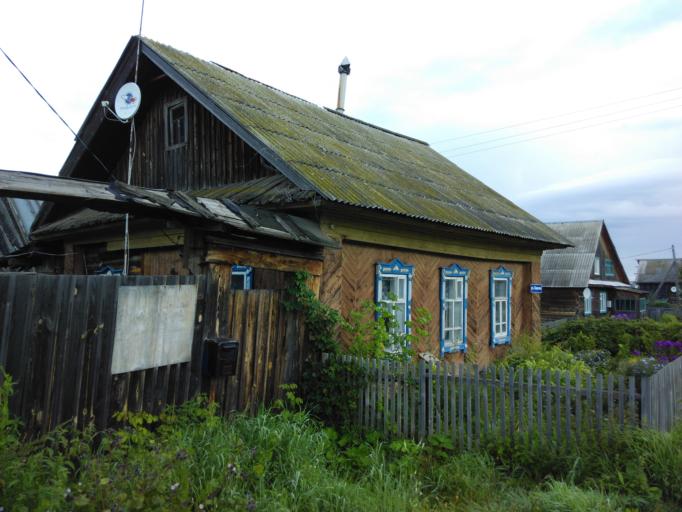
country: RU
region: Perm
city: Foki
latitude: 56.6958
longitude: 54.3517
